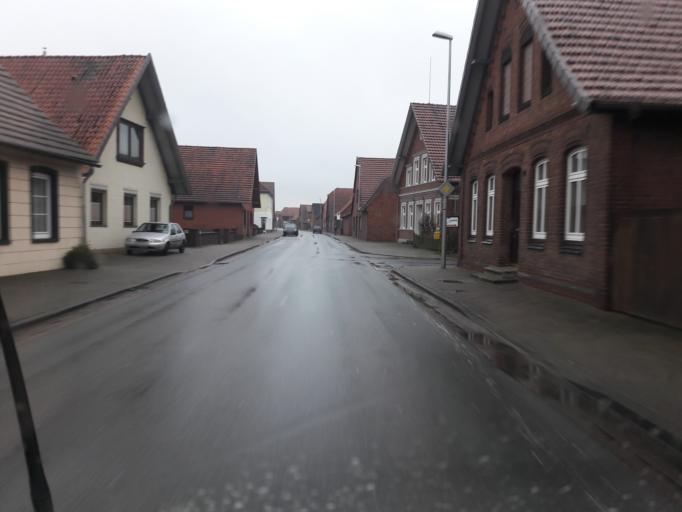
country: DE
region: Lower Saxony
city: Uchte
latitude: 52.4956
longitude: 8.8997
